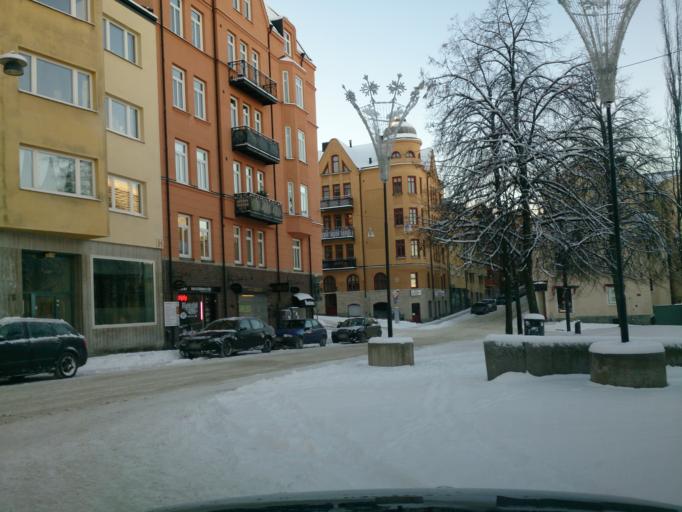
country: SE
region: OEstergoetland
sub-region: Norrkopings Kommun
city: Norrkoping
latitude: 58.5866
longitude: 16.1856
